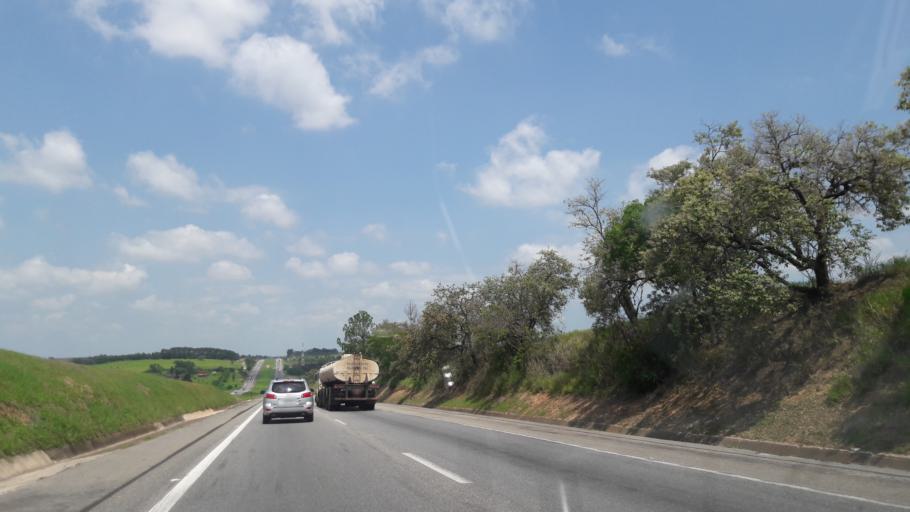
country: BR
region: Sao Paulo
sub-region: Sorocaba
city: Sorocaba
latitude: -23.3748
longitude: -47.4290
